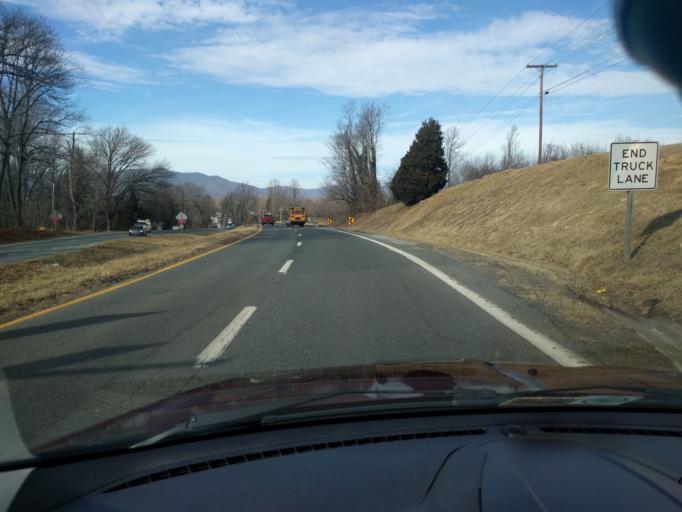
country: US
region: Virginia
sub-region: Amherst County
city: Madison Heights
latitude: 37.4928
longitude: -79.1246
